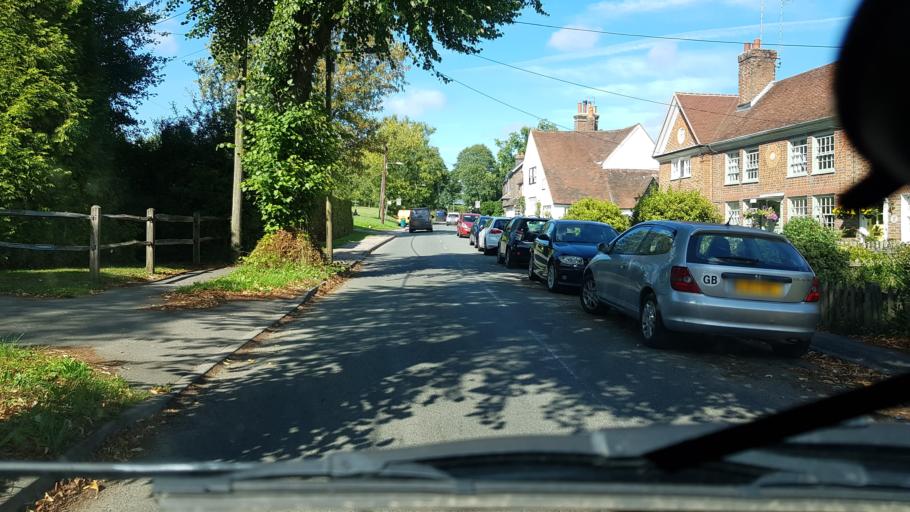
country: GB
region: England
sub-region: West Sussex
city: Horsham
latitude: 51.0916
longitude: -0.3465
